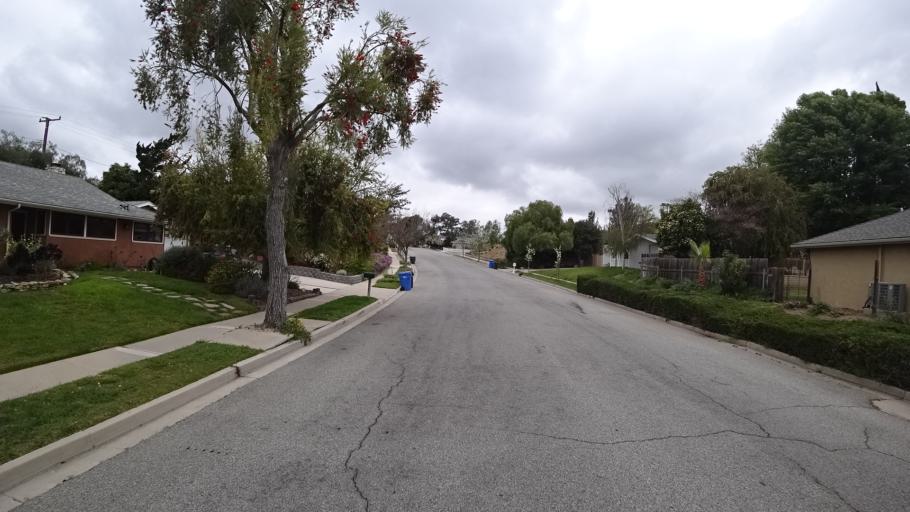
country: US
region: California
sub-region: Ventura County
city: Thousand Oaks
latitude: 34.2110
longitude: -118.8782
